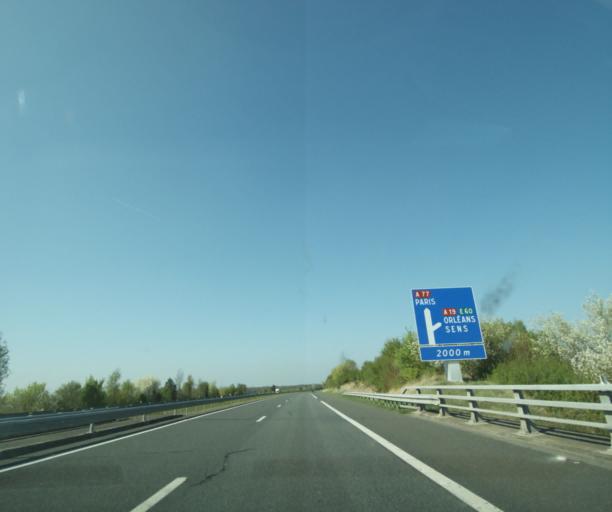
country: FR
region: Centre
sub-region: Departement du Loiret
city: Pannes
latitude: 48.0379
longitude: 2.6725
